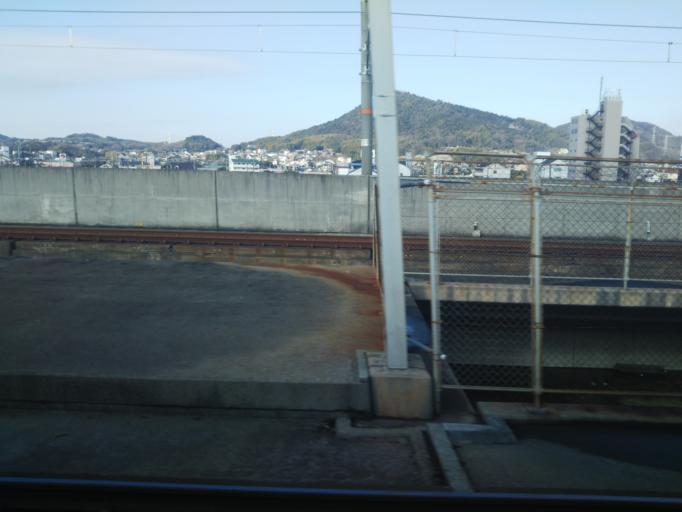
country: JP
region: Okayama
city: Kurashiki
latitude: 34.4613
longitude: 133.8074
